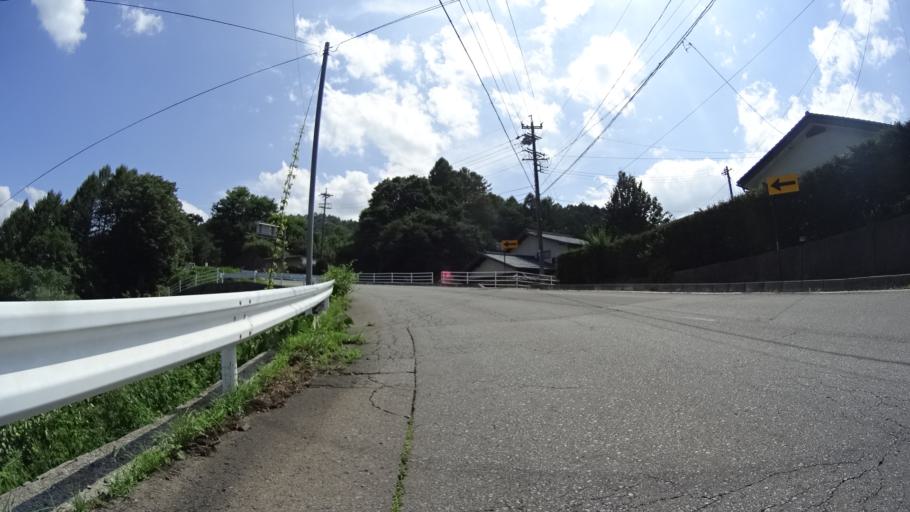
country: JP
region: Nagano
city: Saku
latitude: 36.0583
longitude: 138.4648
